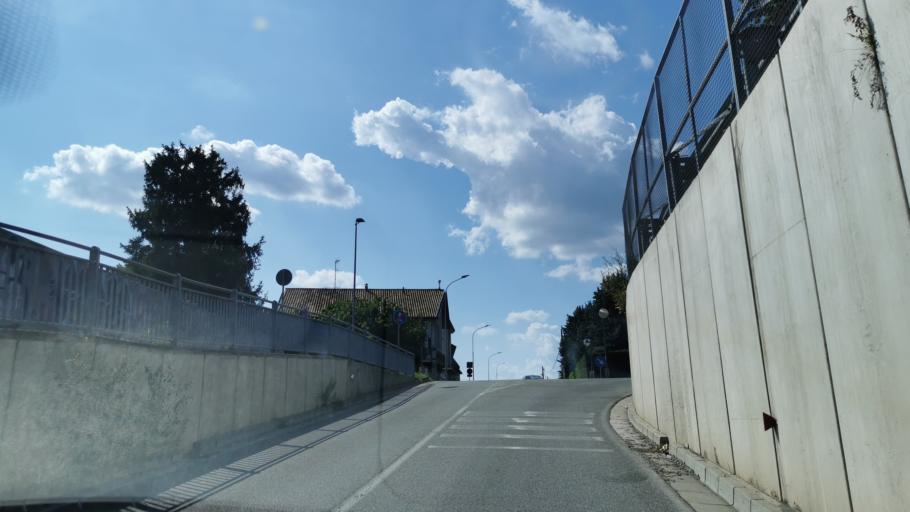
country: IT
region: Lombardy
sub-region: Provincia di Monza e Brianza
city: Cesano Maderno
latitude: 45.6384
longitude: 9.1631
